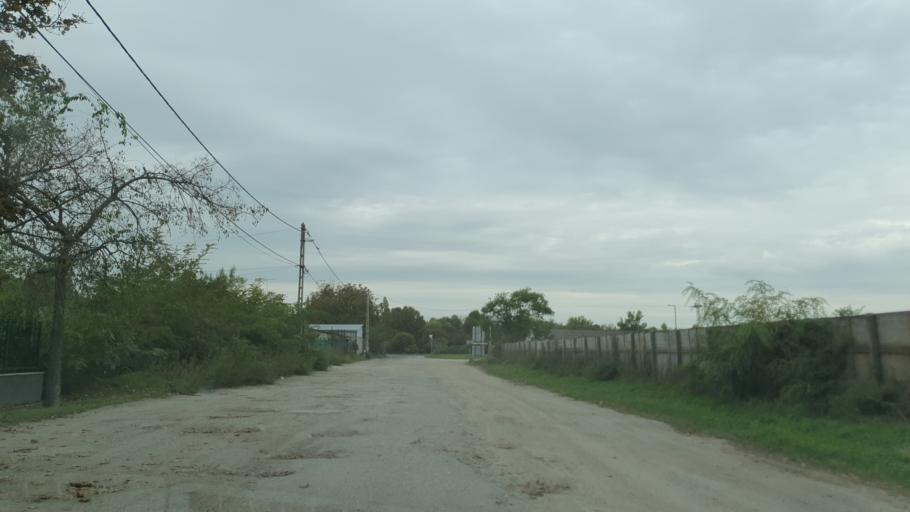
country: HU
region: Budapest
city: Budapest XXI. keruelet
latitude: 47.4022
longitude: 19.0596
